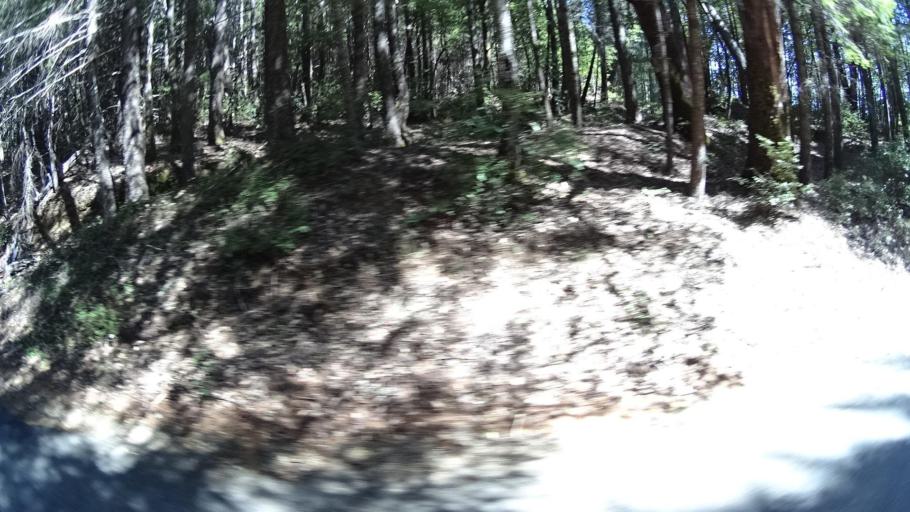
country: US
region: California
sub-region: Humboldt County
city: Redway
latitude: 40.1958
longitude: -124.0973
